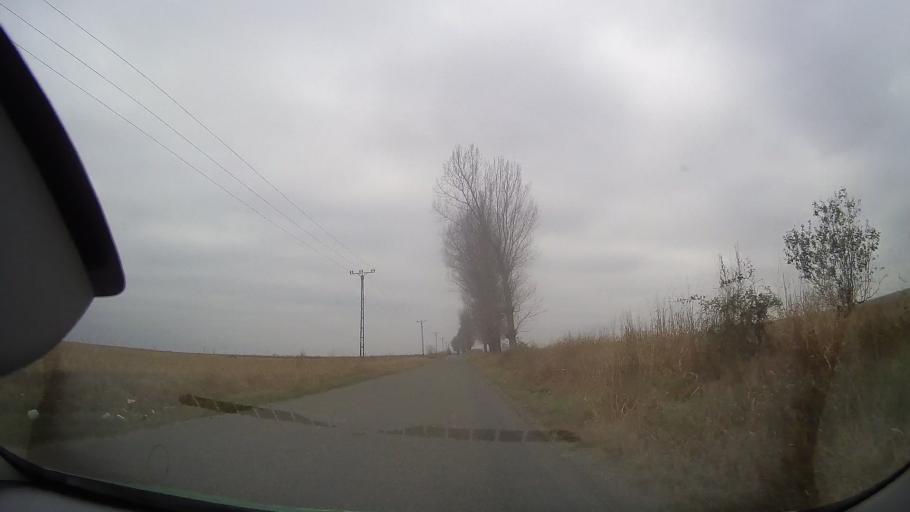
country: RO
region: Buzau
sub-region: Comuna Pogoanele
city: Pogoanele
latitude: 44.9477
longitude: 27.0117
